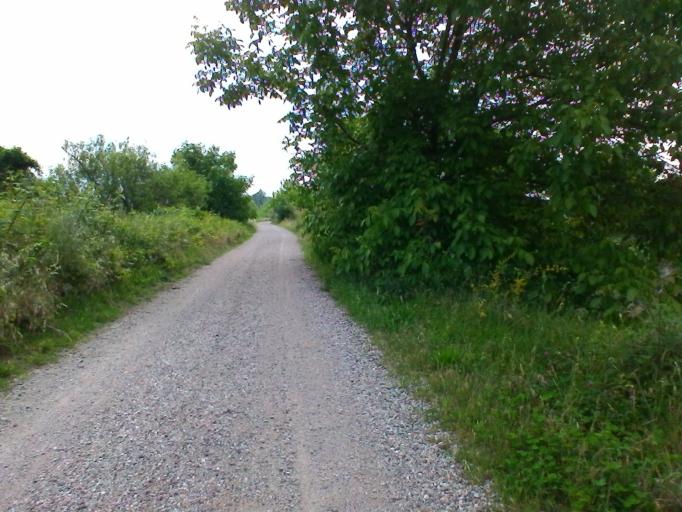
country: IT
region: Lombardy
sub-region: Provincia di Mantova
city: Lunetta-Frassino
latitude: 45.1291
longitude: 10.8216
